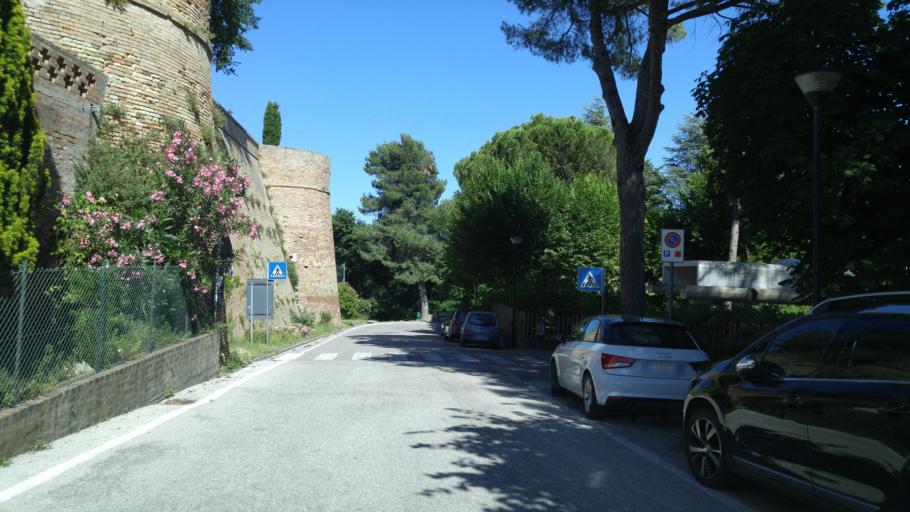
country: IT
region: The Marches
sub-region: Provincia di Pesaro e Urbino
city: Mombaroccio
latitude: 43.7953
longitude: 12.8547
